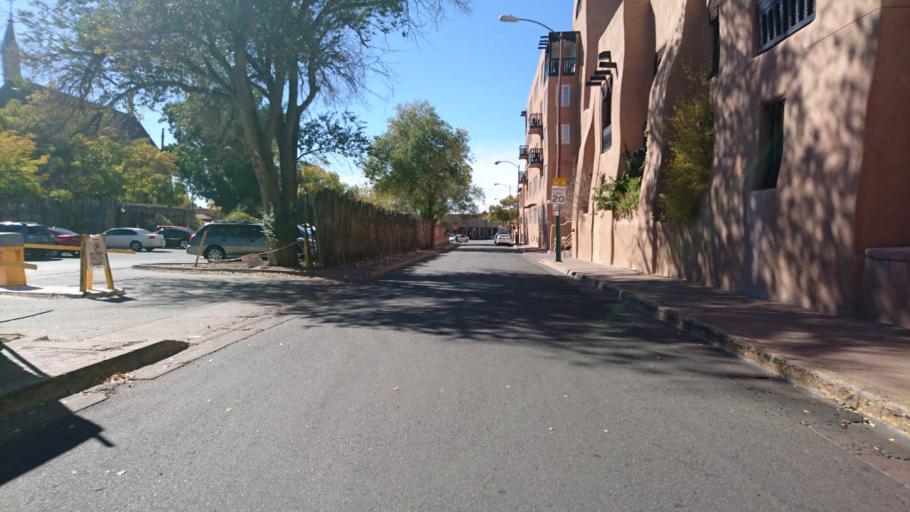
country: US
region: New Mexico
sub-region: Santa Fe County
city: Santa Fe
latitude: 35.6860
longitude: -105.9368
